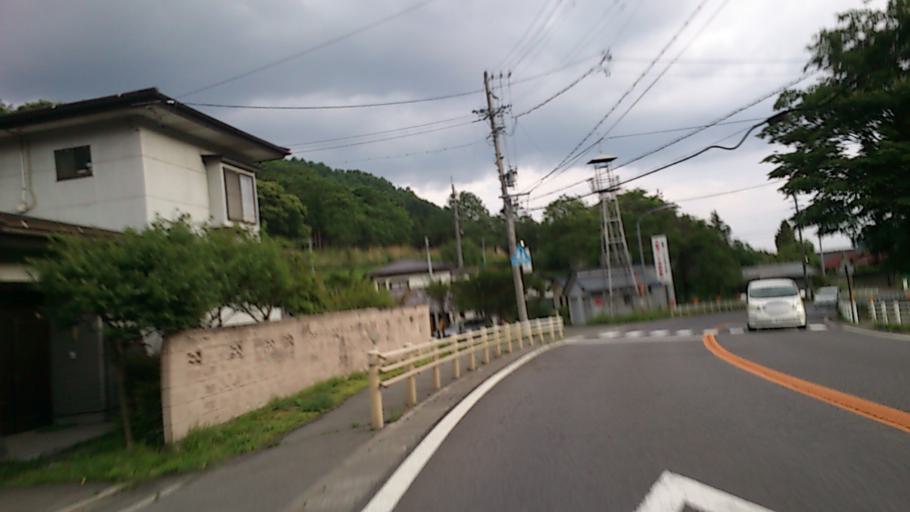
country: JP
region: Nagano
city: Suwa
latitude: 36.1222
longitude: 138.1021
